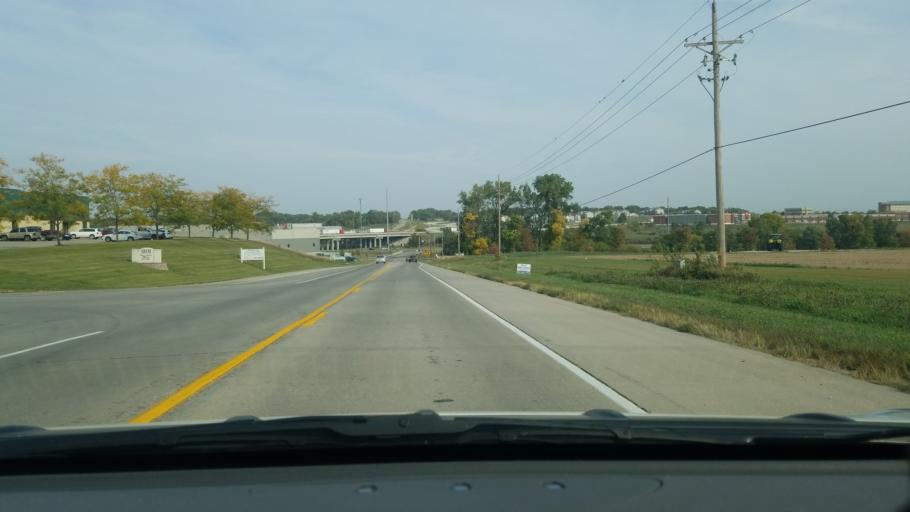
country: US
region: Nebraska
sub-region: Sarpy County
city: Chalco
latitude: 41.1721
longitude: -96.1196
